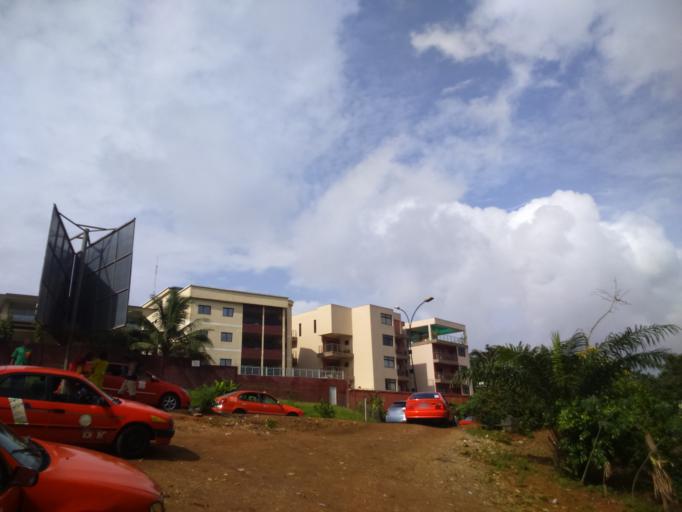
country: CI
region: Lagunes
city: Abidjan
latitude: 5.3486
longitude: -4.0041
